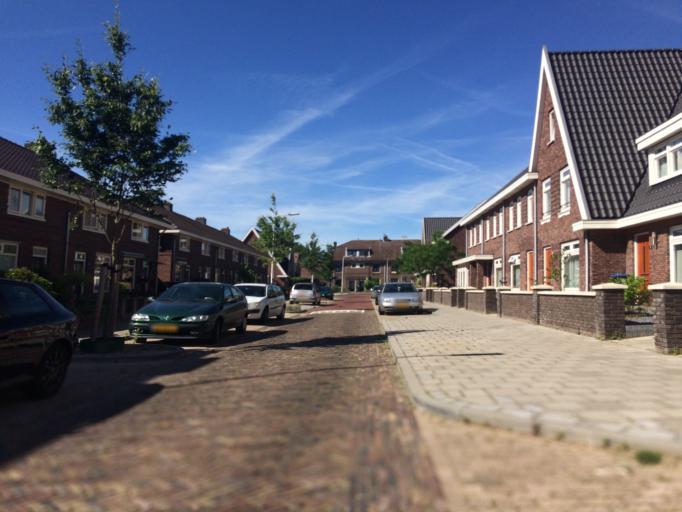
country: NL
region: Gelderland
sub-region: Gemeente Nijmegen
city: Nijmegen
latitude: 51.8348
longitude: 5.8512
